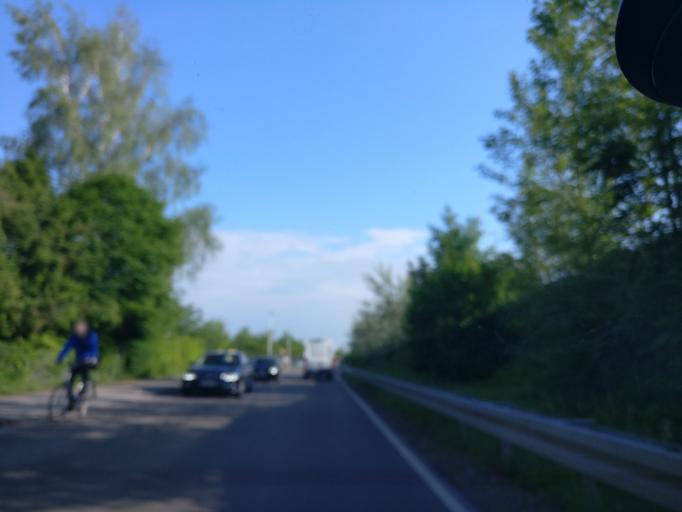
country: DE
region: Bavaria
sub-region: Upper Bavaria
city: Karlsfeld
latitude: 48.2160
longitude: 11.4575
